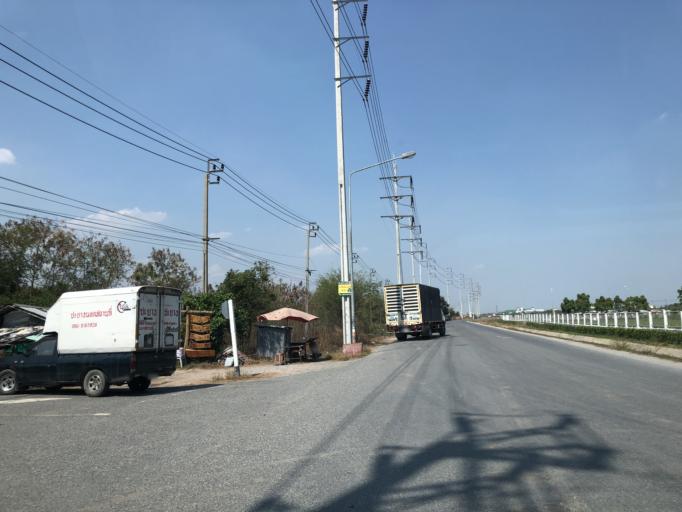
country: TH
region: Samut Prakan
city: Bang Bo District
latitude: 13.5061
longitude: 100.7438
